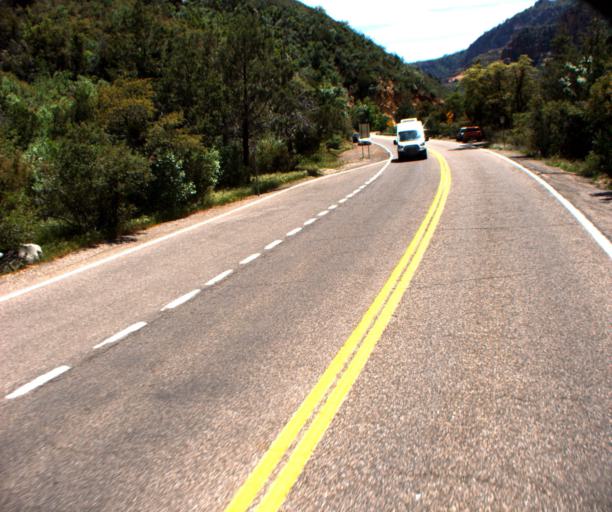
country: US
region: Arizona
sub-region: Coconino County
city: Sedona
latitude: 34.9555
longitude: -111.7547
